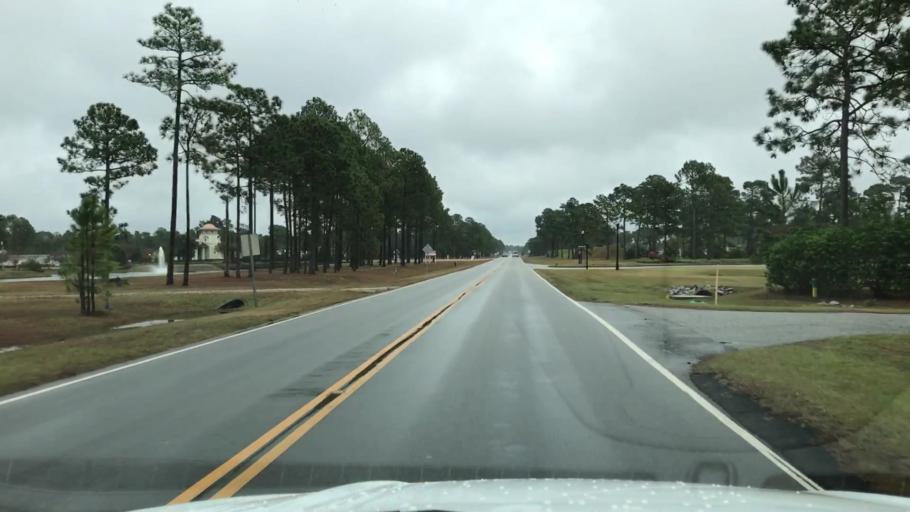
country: US
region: South Carolina
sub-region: Horry County
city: Forestbrook
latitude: 33.7572
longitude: -78.9103
